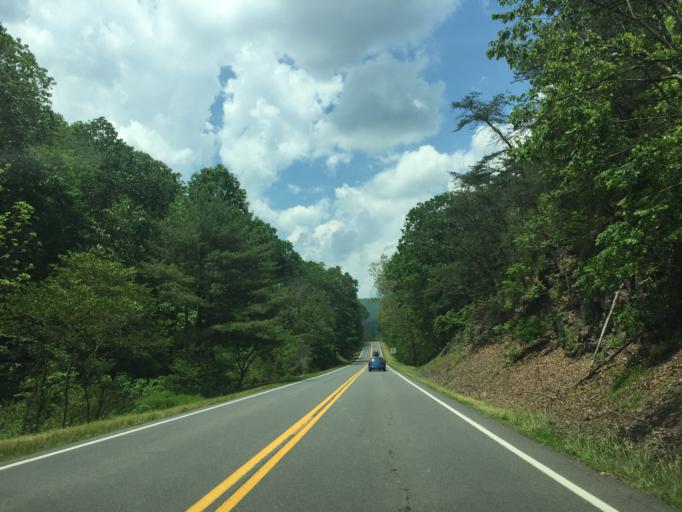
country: US
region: Virginia
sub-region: Shenandoah County
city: Strasburg
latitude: 39.0826
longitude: -78.4265
